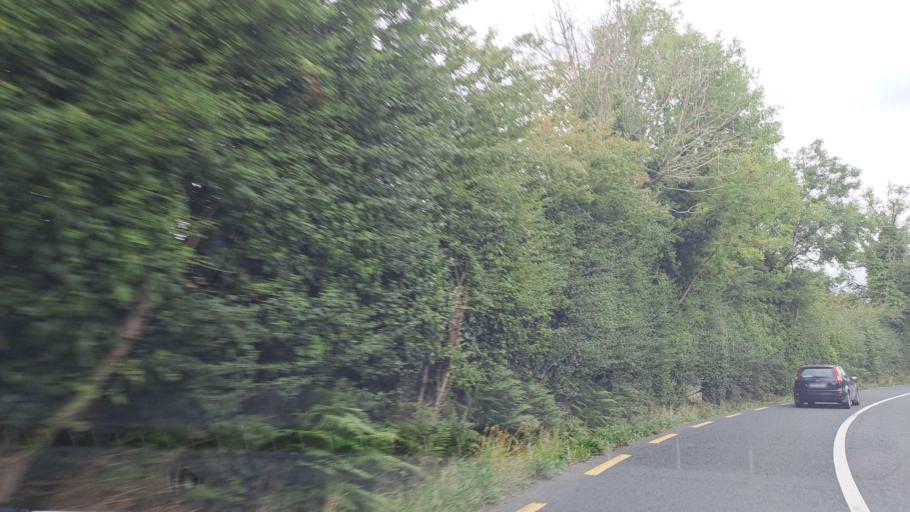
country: IE
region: Ulster
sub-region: An Cabhan
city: Bailieborough
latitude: 53.9912
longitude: -6.9002
